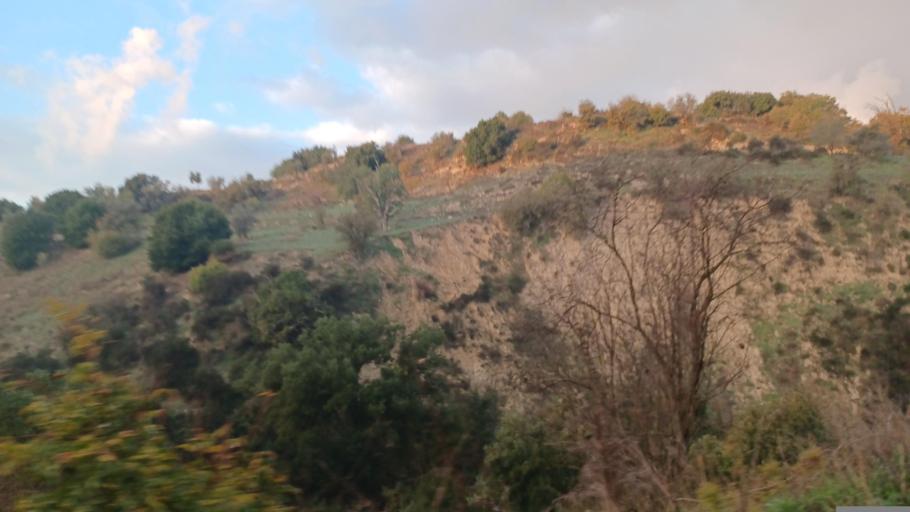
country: CY
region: Pafos
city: Mesogi
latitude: 34.8485
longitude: 32.5195
